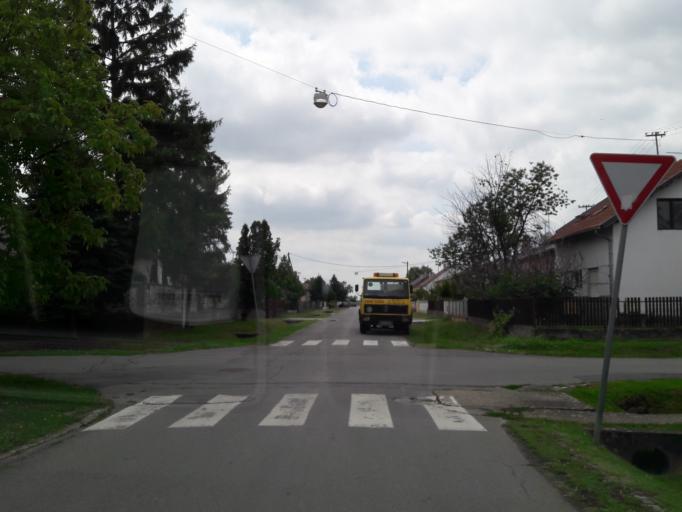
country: HR
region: Osjecko-Baranjska
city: Tenja
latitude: 45.5111
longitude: 18.7349
